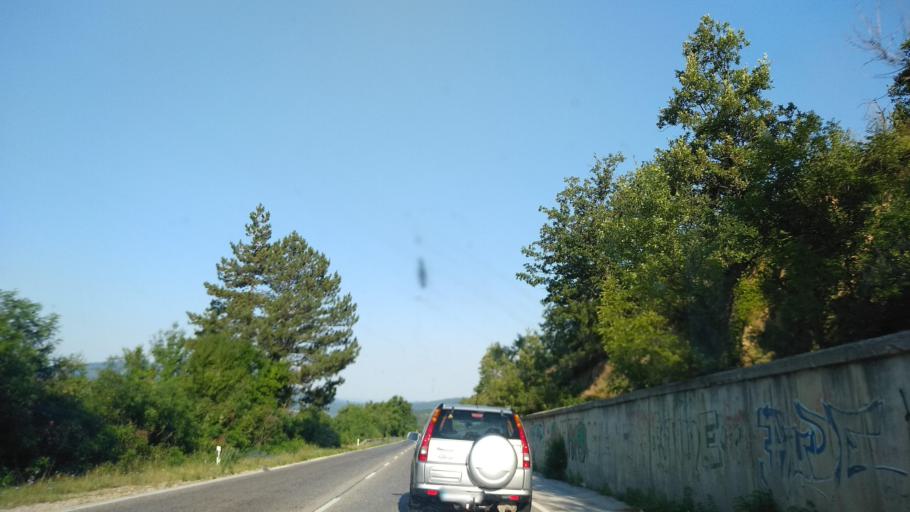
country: BG
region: Lovech
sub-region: Obshtina Lovech
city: Lovech
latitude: 43.0478
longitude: 24.7845
